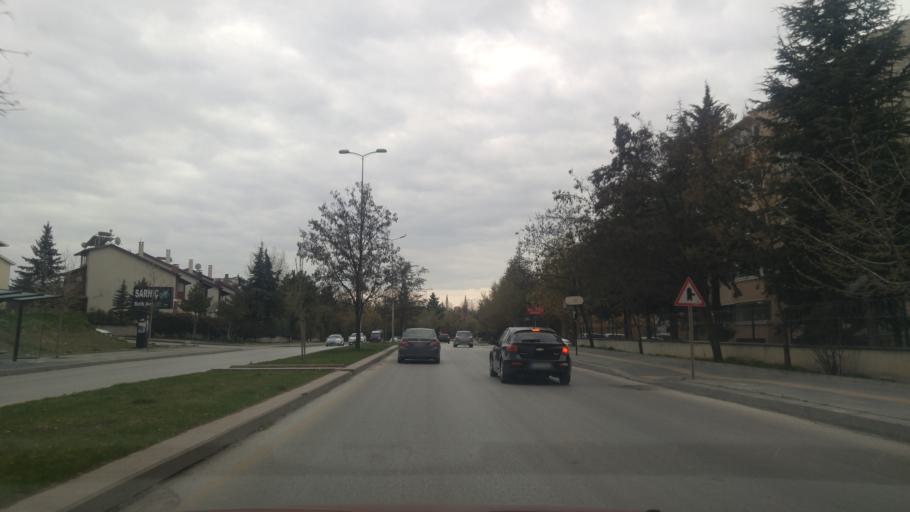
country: TR
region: Ankara
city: Etimesgut
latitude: 39.8806
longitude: 32.6895
